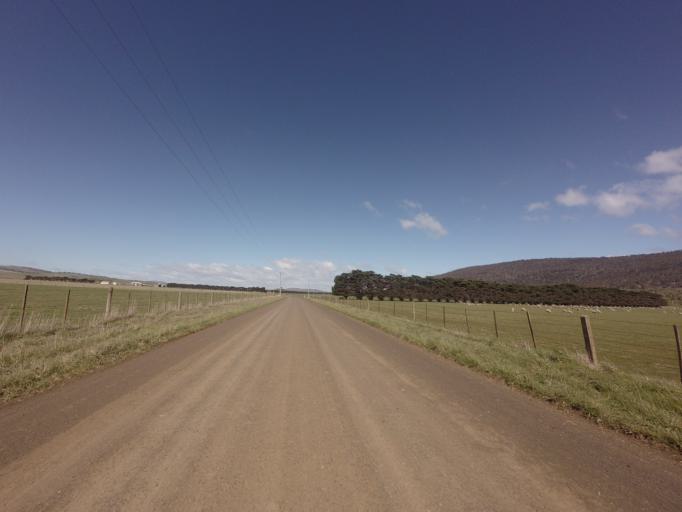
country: AU
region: Tasmania
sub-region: Northern Midlands
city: Evandale
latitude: -41.9561
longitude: 147.4365
